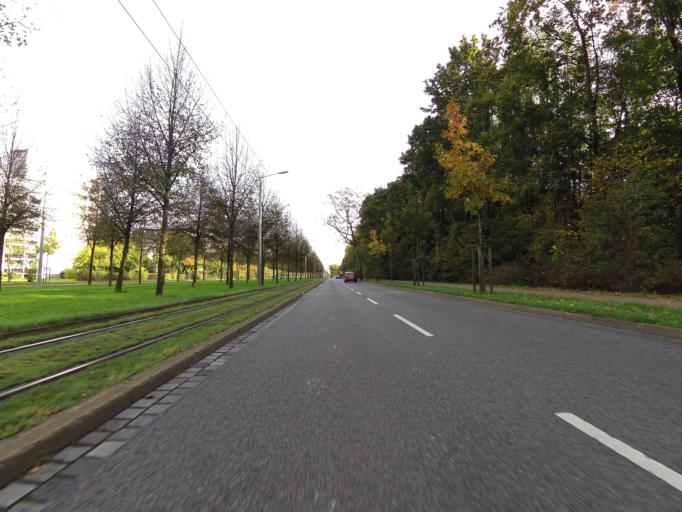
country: DE
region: Saxony
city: Dresden
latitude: 51.0430
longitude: 13.7627
